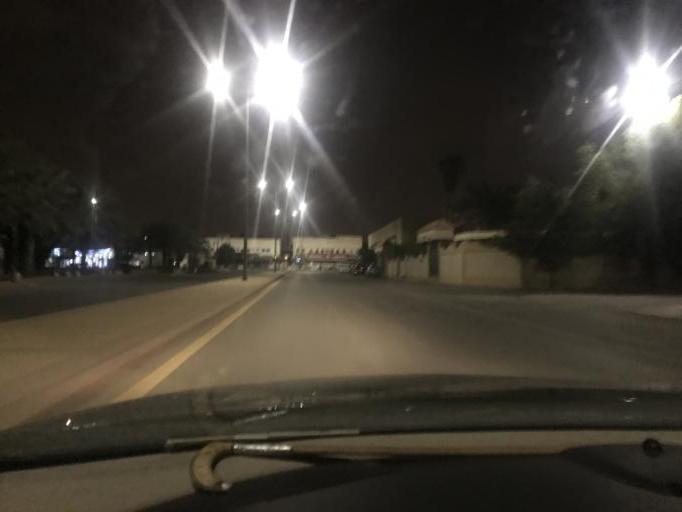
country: SA
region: Ar Riyad
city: Riyadh
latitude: 24.7325
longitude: 46.7765
